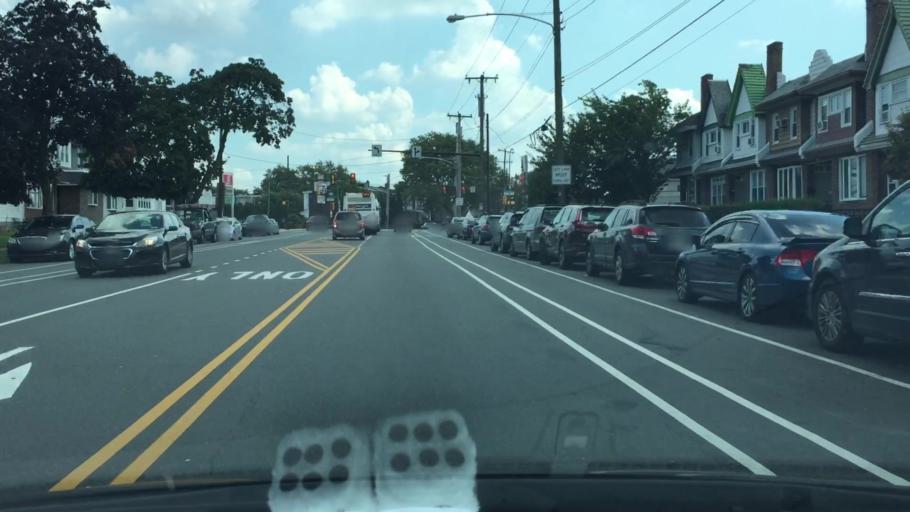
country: US
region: New Jersey
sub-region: Burlington County
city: Palmyra
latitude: 40.0343
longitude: -75.0480
